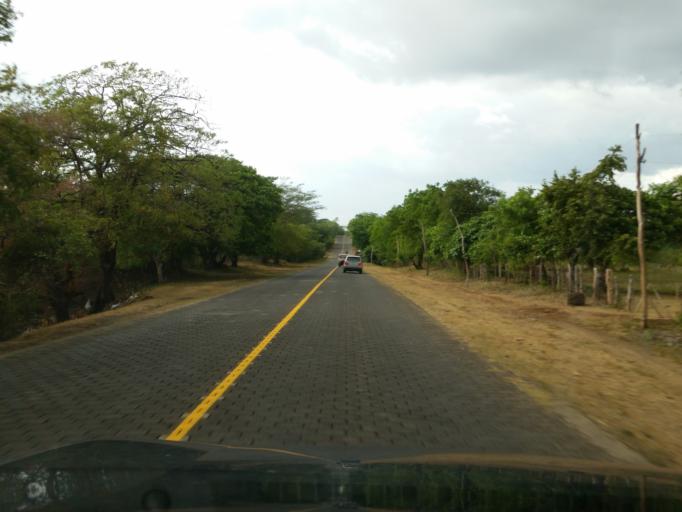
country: NI
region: Managua
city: Carlos Fonseca Amador
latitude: 11.9744
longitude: -86.5143
